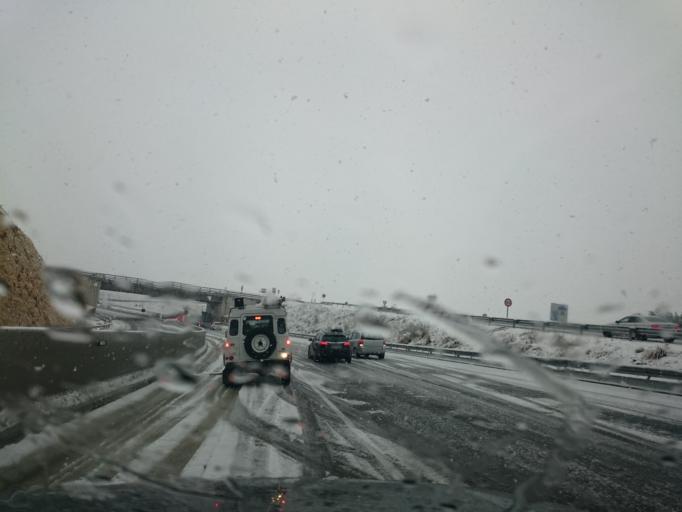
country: ES
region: Catalonia
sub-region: Provincia de Barcelona
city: Vilafranca del Penedes
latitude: 41.3204
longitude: 1.7262
